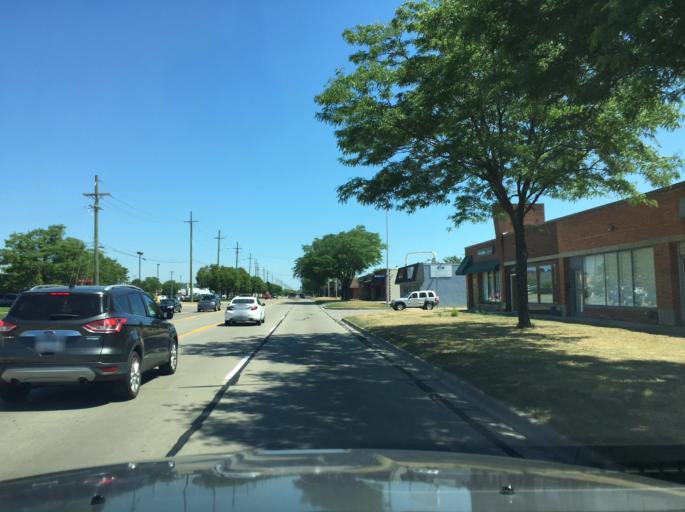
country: US
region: Michigan
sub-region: Wayne County
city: Grosse Pointe Woods
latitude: 42.4700
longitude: -82.9060
